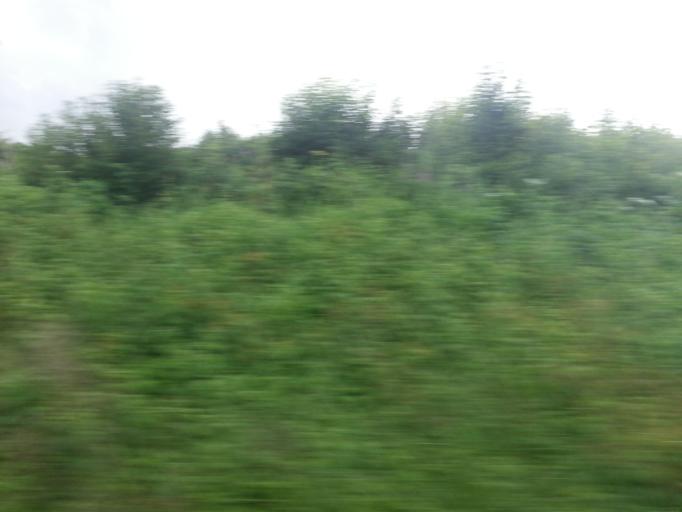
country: NO
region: Sor-Trondelag
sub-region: Trondheim
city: Trondheim
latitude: 63.4294
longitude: 10.5146
